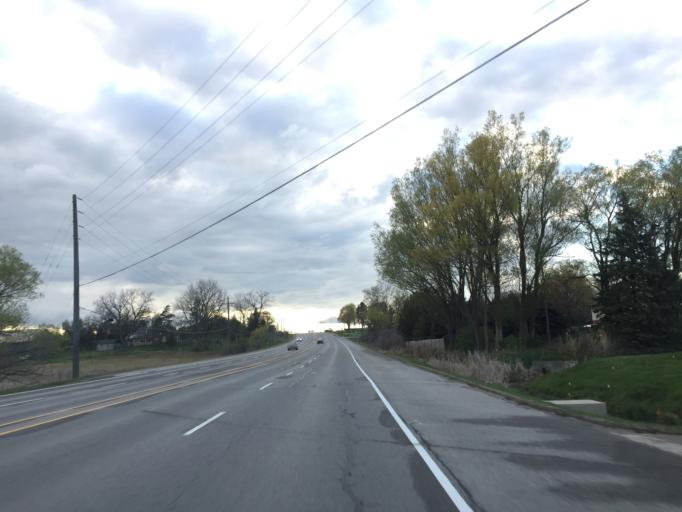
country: CA
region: Ontario
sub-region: Wellington County
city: Guelph
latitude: 43.5780
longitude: -80.2877
